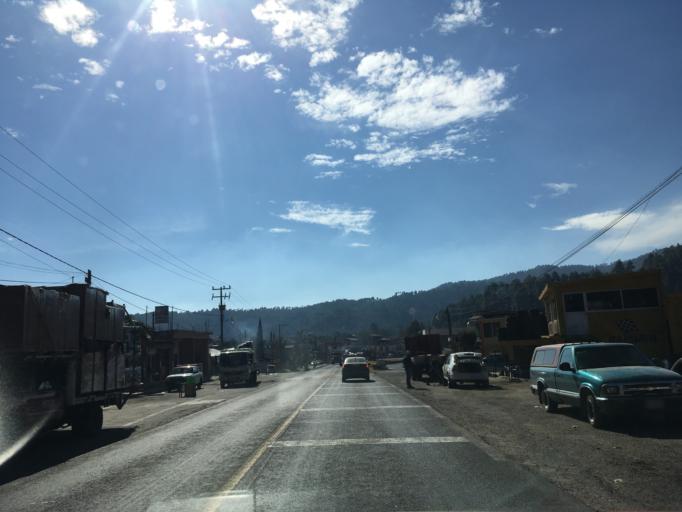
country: MX
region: Michoacan
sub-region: Hidalgo
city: Tierras Coloradas (San Pedro)
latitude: 19.6841
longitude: -100.7408
